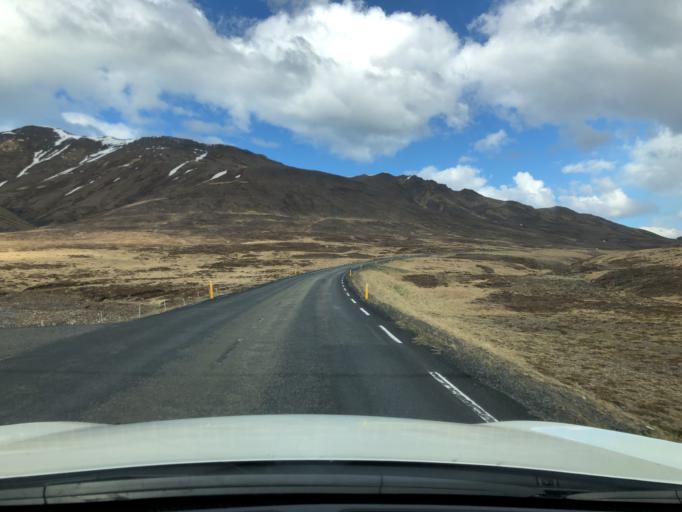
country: IS
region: West
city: Stykkisholmur
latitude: 64.9647
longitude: -23.0219
